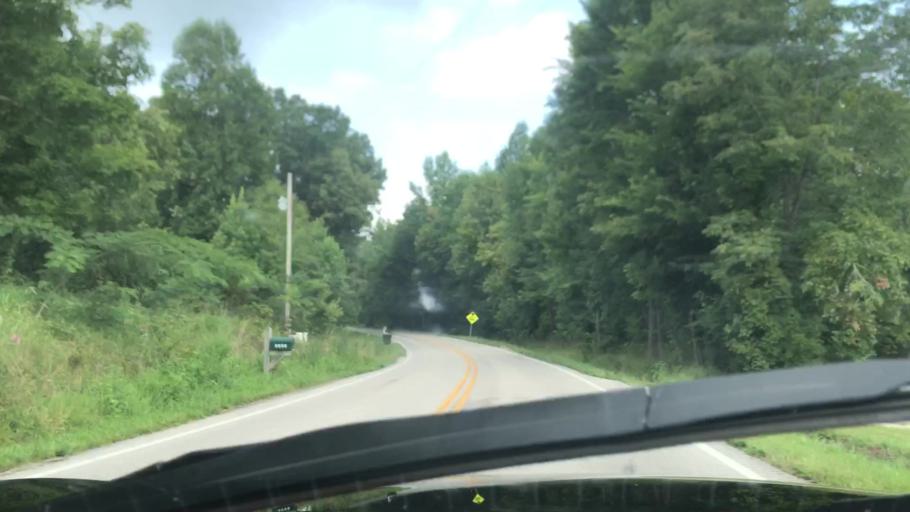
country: US
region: Kentucky
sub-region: Butler County
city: Morgantown
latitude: 37.1744
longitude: -86.8385
